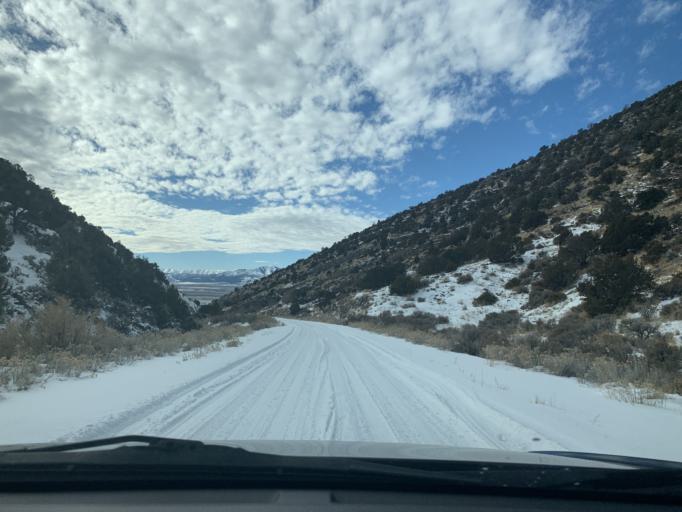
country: US
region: Utah
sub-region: Tooele County
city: Tooele
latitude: 40.3127
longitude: -112.2416
